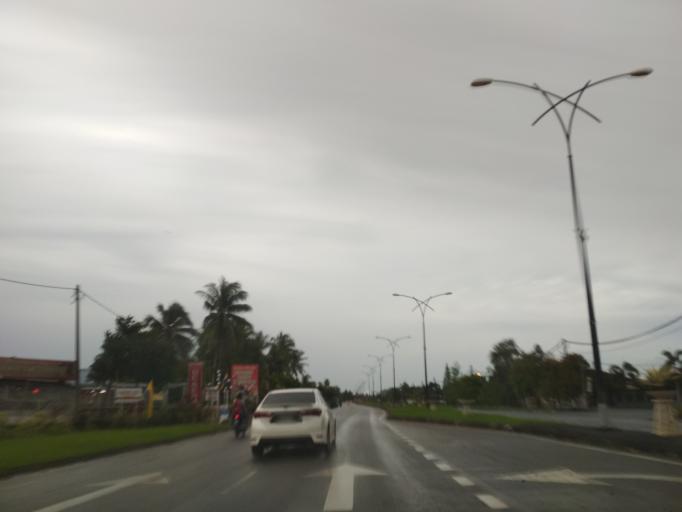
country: MY
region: Perlis
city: Kangar
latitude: 6.4585
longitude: 100.2078
